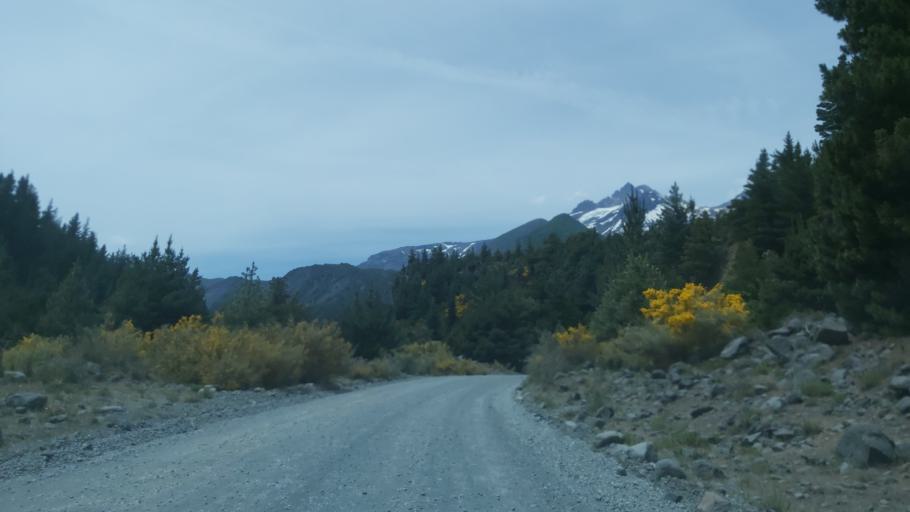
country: AR
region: Neuquen
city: Las Ovejas
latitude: -37.3898
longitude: -71.4671
